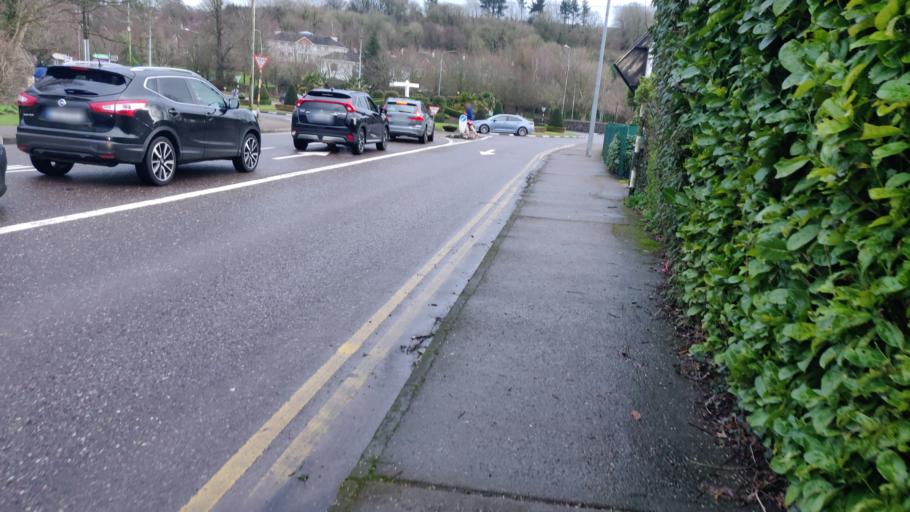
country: IE
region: Munster
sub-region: County Cork
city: Cork
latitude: 51.8765
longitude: -8.4323
